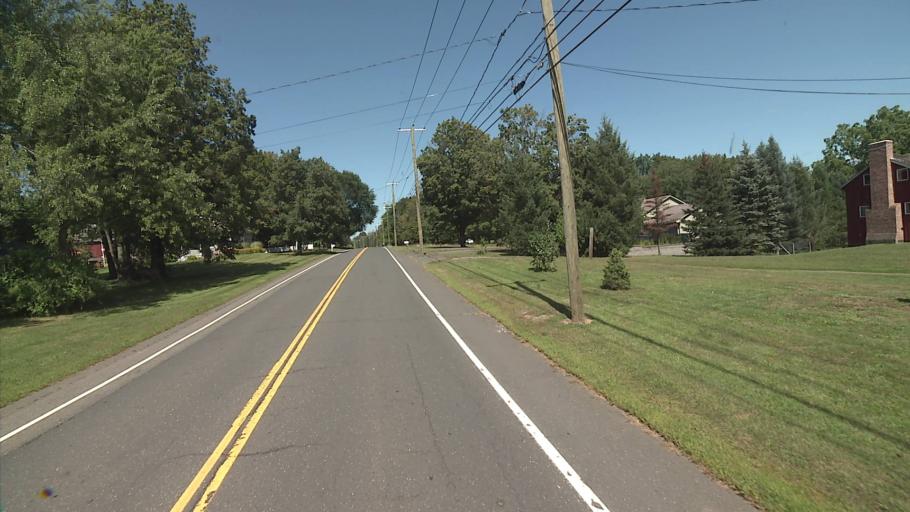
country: US
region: Connecticut
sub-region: Hartford County
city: Enfield
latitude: 41.9705
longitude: -72.6147
